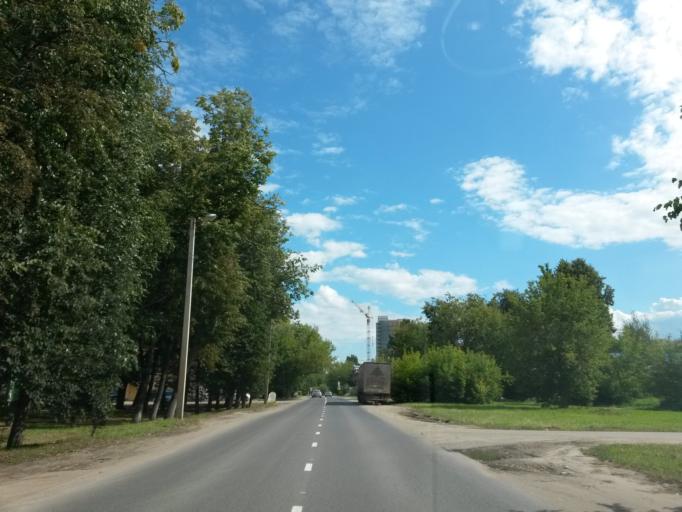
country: RU
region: Ivanovo
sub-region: Gorod Ivanovo
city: Ivanovo
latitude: 56.9899
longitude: 40.9734
